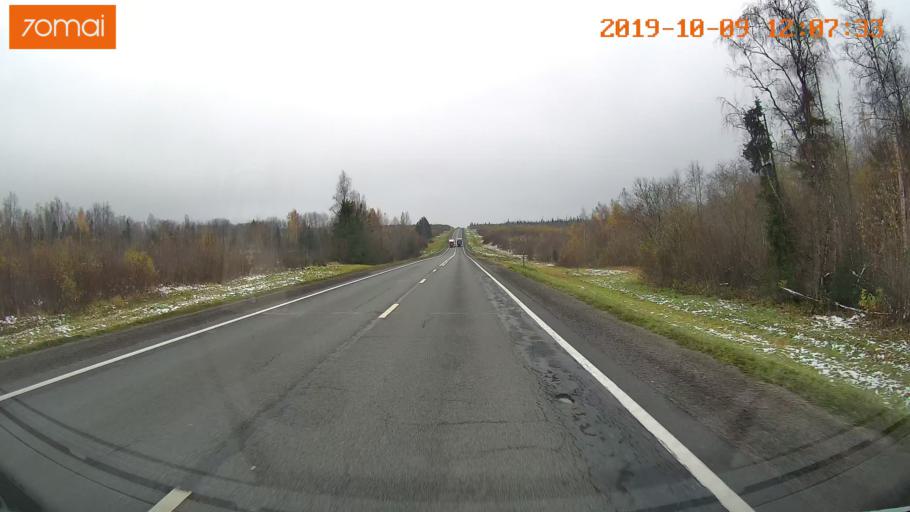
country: RU
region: Jaroslavl
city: Prechistoye
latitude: 58.5979
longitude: 40.3426
